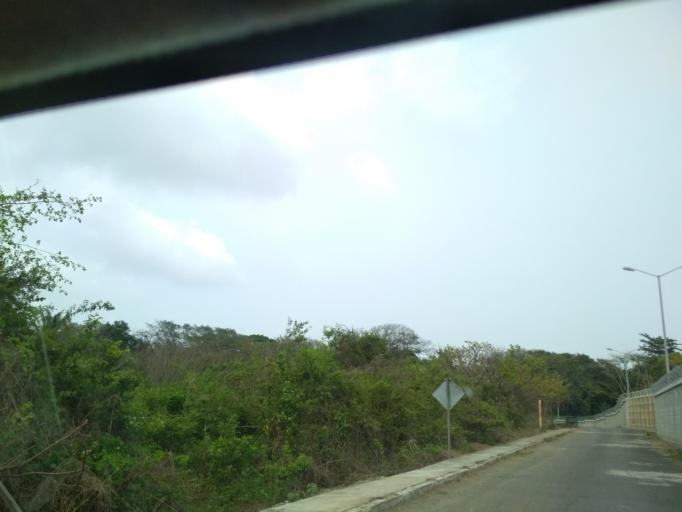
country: MX
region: Veracruz
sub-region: Medellin
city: Fraccionamiento Arboledas San Ramon
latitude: 19.0900
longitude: -96.1461
